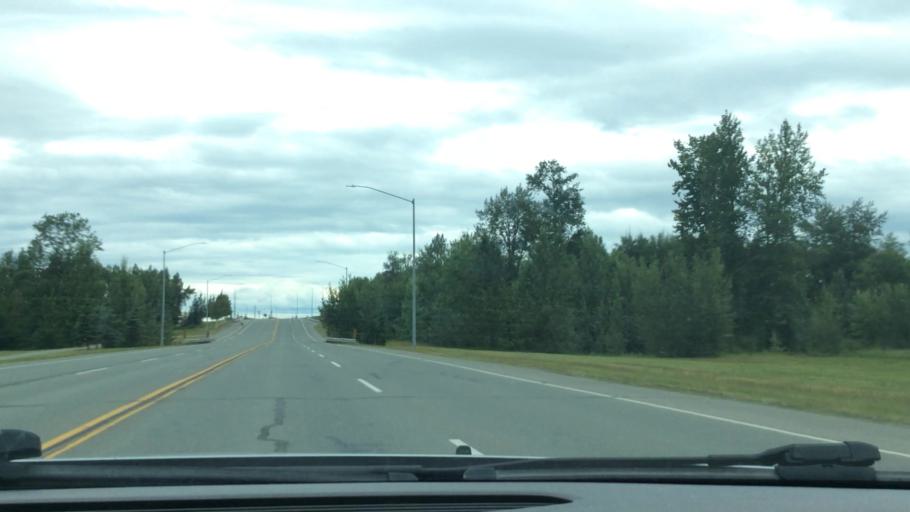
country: US
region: Alaska
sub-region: Anchorage Municipality
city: Anchorage
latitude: 61.2361
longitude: -149.7785
